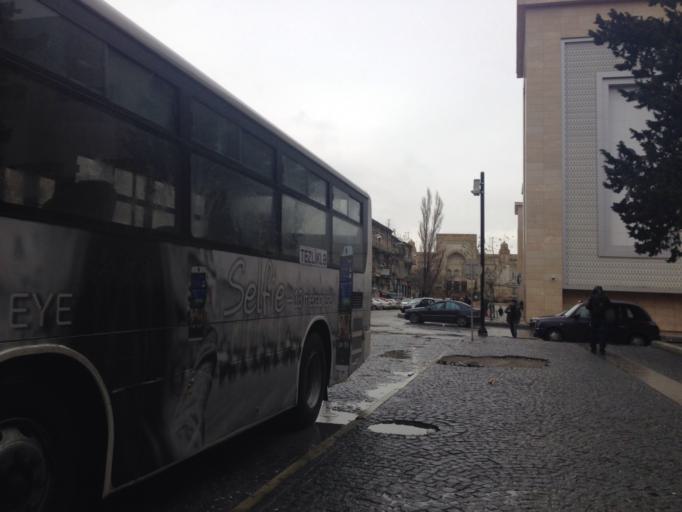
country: AZ
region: Baki
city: Baku
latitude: 40.3792
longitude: 49.8455
